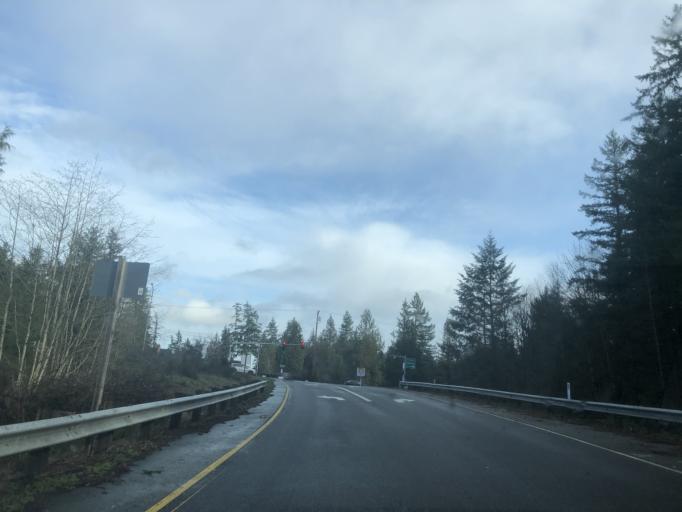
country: US
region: Washington
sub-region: Kitsap County
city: Poulsbo
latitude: 47.7519
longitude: -122.6636
